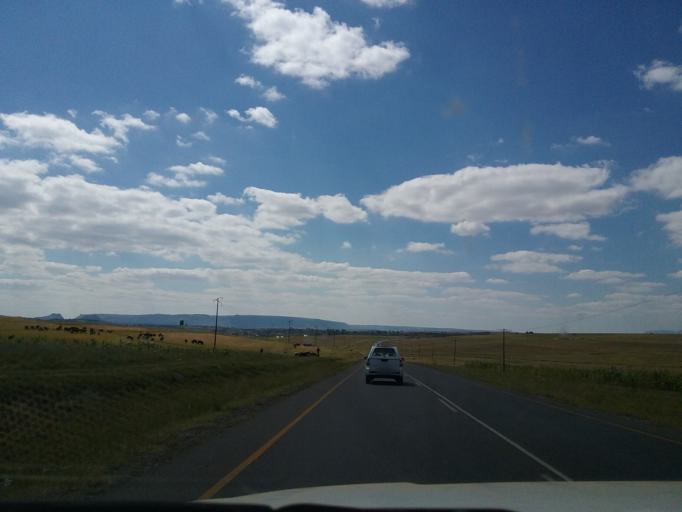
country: LS
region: Maseru
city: Maseru
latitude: -29.4721
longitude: 27.5325
